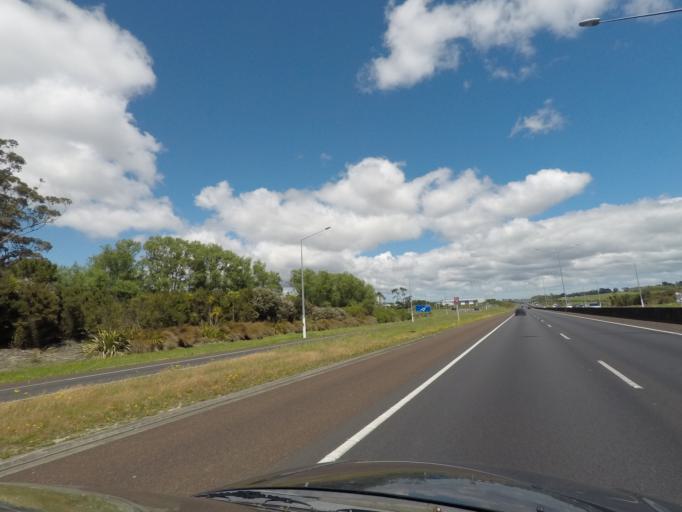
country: NZ
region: Auckland
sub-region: Auckland
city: Rosebank
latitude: -36.7981
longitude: 174.6419
